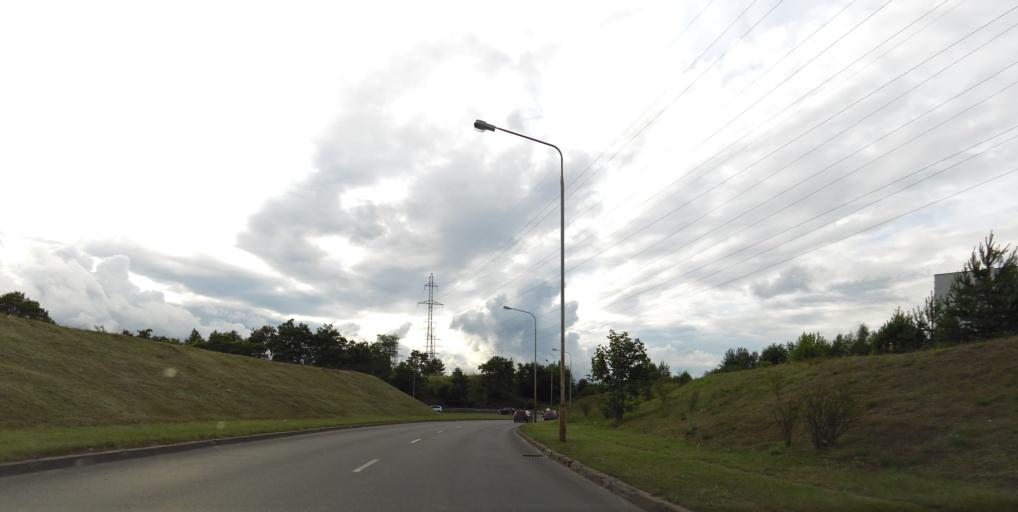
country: LT
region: Vilnius County
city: Justiniskes
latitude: 54.7064
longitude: 25.2111
